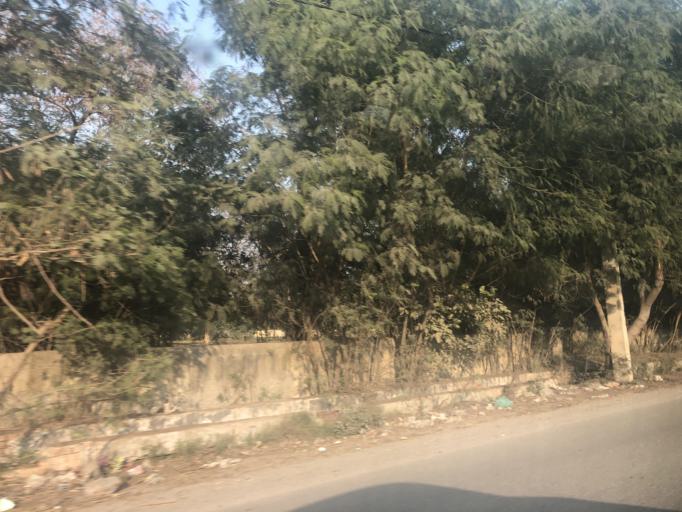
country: IN
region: Haryana
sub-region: Gurgaon
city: Gurgaon
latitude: 28.5415
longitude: 77.0209
